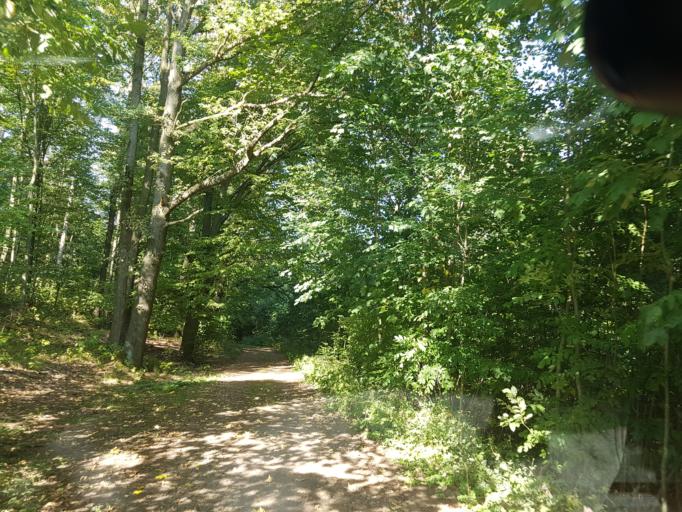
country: DE
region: Saxony
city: Kriebstein
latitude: 51.0446
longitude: 13.0137
